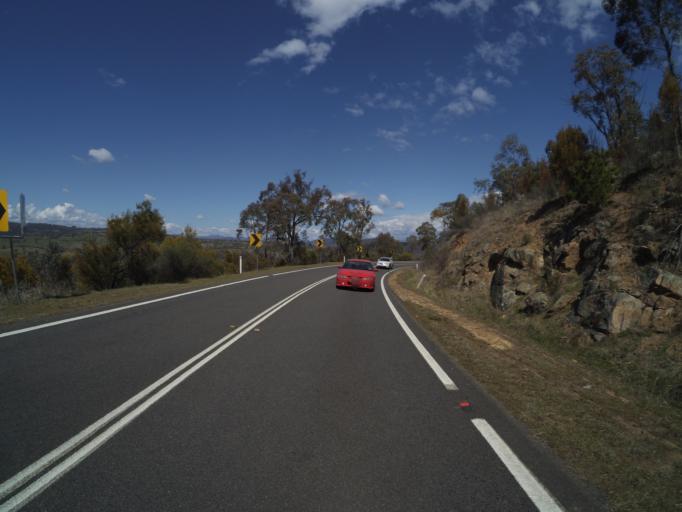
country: AU
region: Australian Capital Territory
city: Macquarie
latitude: -35.3104
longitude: 148.9509
